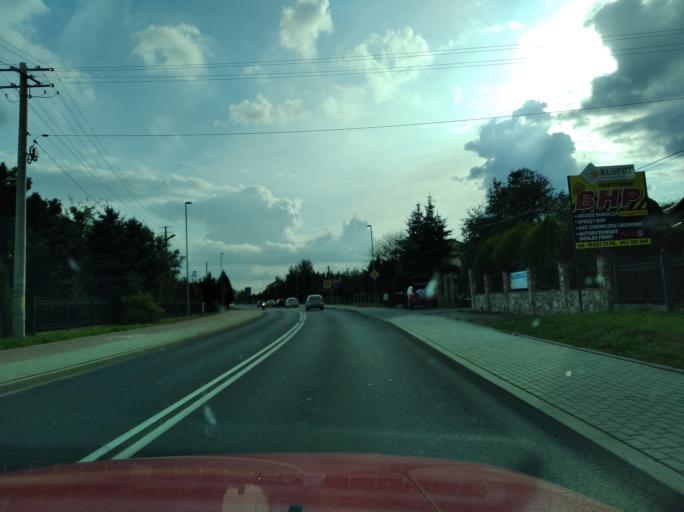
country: PL
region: Subcarpathian Voivodeship
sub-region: Powiat jaroslawski
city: Pawlosiow
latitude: 49.9955
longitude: 22.6664
